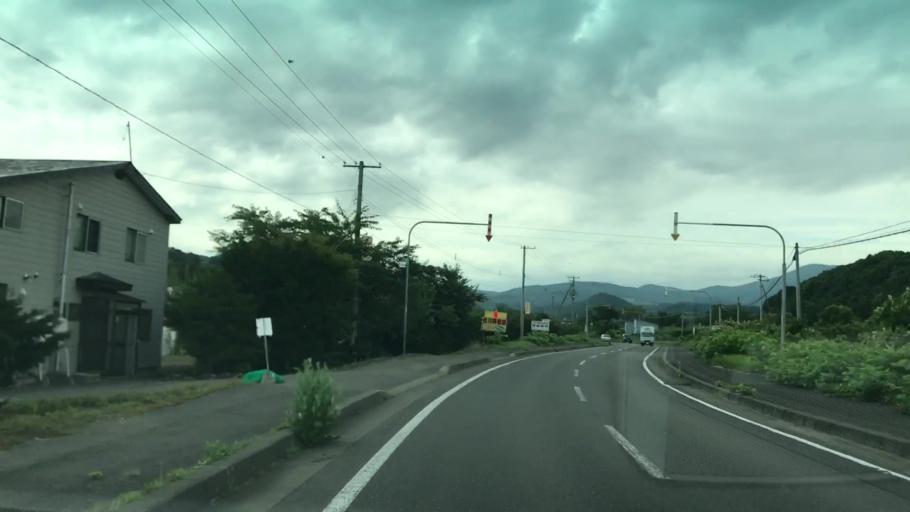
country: JP
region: Hokkaido
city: Yoichi
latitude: 43.1754
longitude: 140.8219
